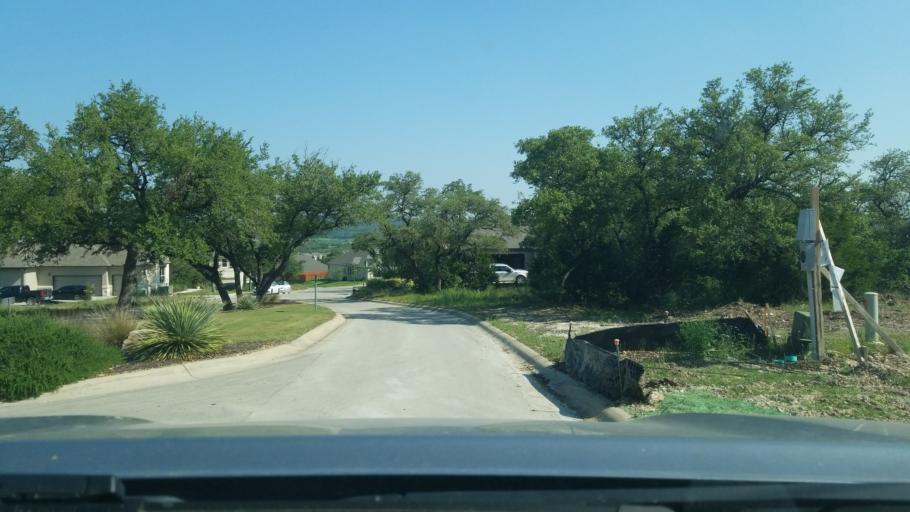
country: US
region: Texas
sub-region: Comal County
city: Bulverde
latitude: 29.7619
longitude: -98.4213
